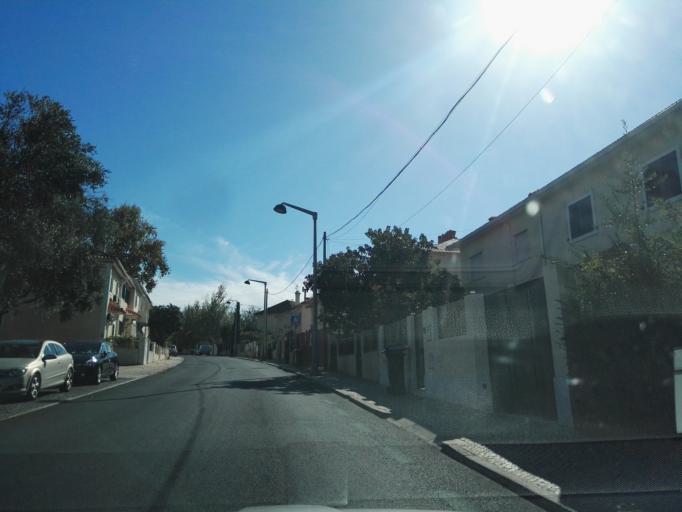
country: PT
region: Lisbon
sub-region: Loures
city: Moscavide
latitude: 38.7761
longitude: -9.1179
